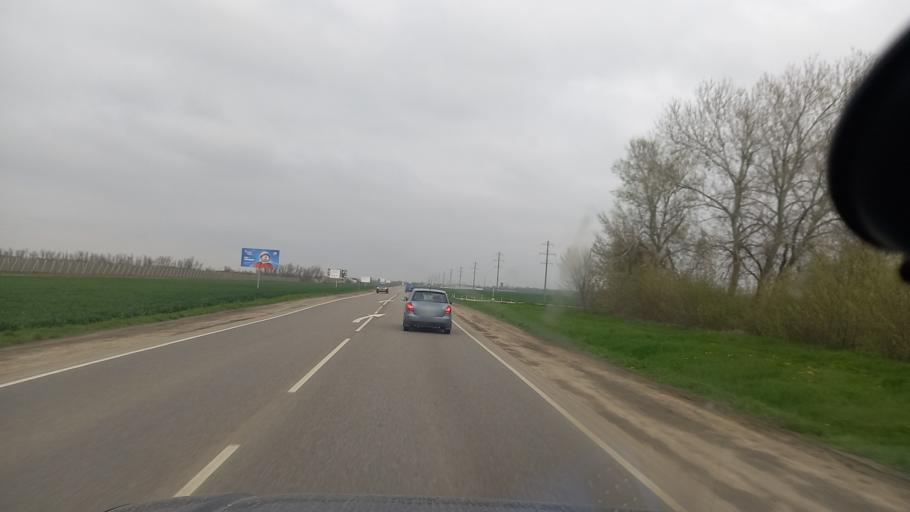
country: RU
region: Krasnodarskiy
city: Slavyansk-na-Kubani
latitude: 45.2450
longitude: 38.0482
